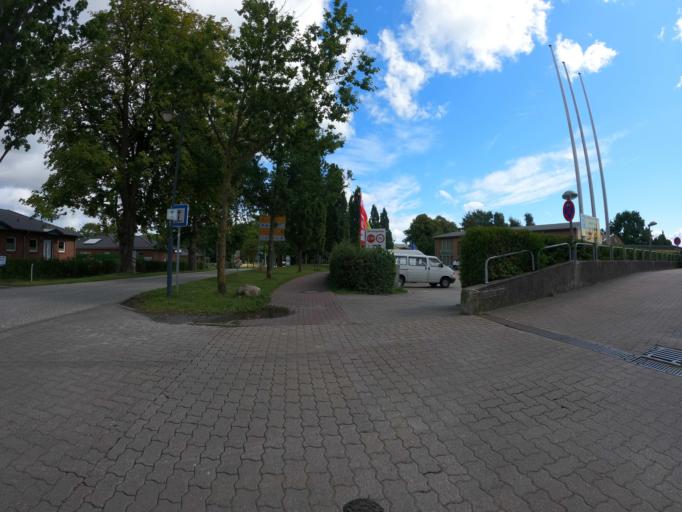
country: DE
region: Mecklenburg-Vorpommern
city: Putbus
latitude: 54.3465
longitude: 13.4982
